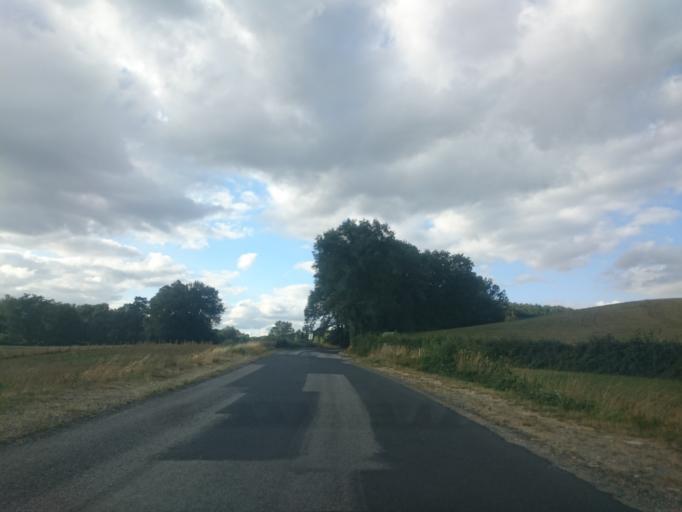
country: FR
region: Auvergne
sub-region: Departement du Cantal
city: Saint-Mamet-la-Salvetat
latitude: 44.8622
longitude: 2.2249
